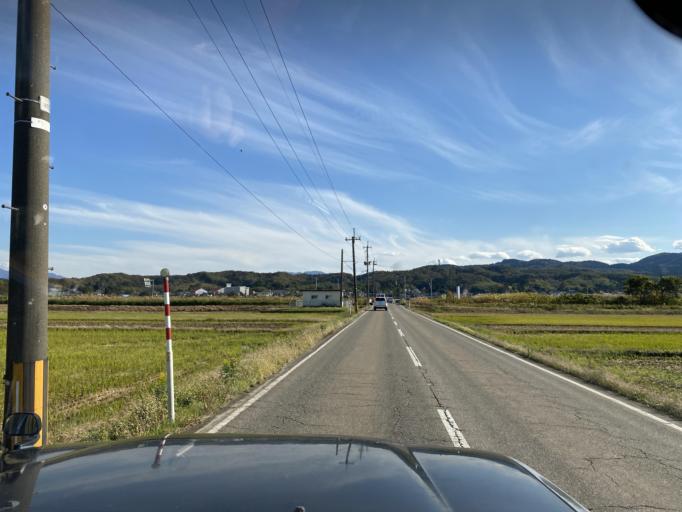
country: JP
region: Niigata
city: Niitsu-honcho
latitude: 37.7570
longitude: 139.0901
